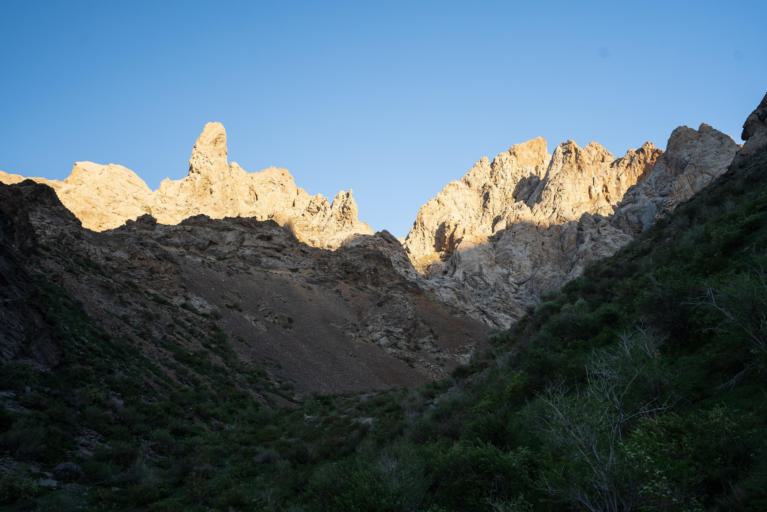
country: KZ
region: Ongtustik Qazaqstan
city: Ashchysay
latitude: 43.7710
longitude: 68.7774
